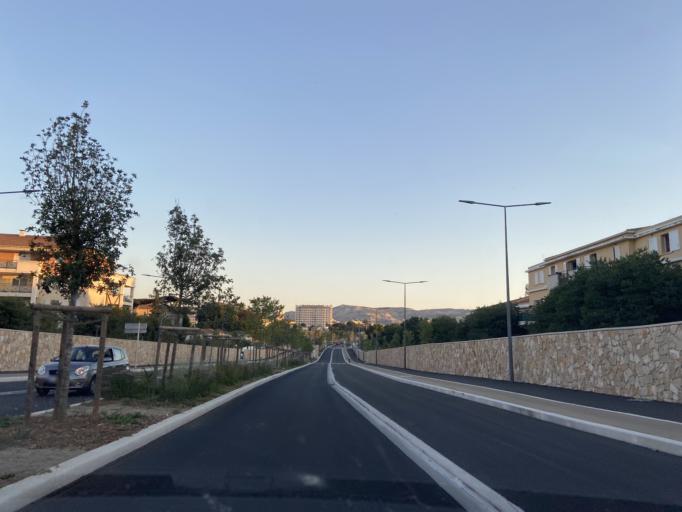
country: FR
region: Provence-Alpes-Cote d'Azur
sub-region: Departement des Bouches-du-Rhone
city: Marseille 10
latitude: 43.2674
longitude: 5.4200
